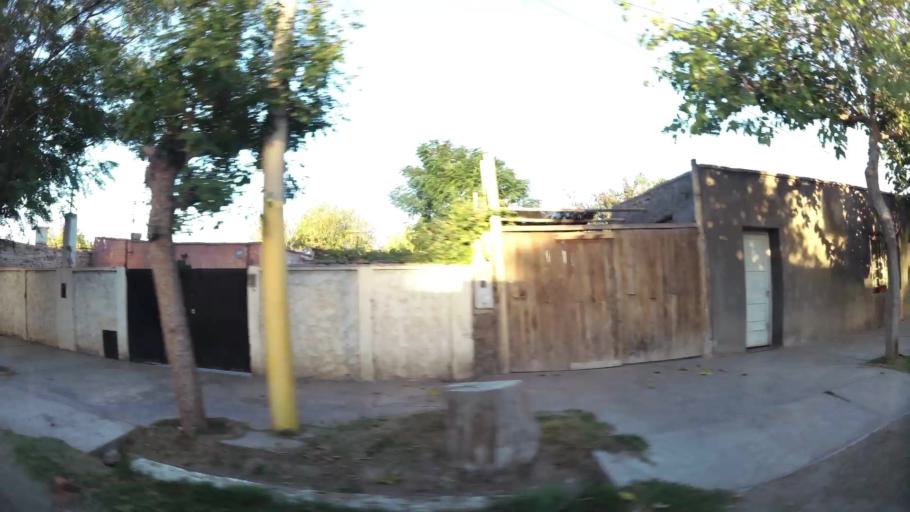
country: AR
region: San Juan
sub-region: Departamento de Santa Lucia
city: Santa Lucia
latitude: -31.5244
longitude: -68.5075
